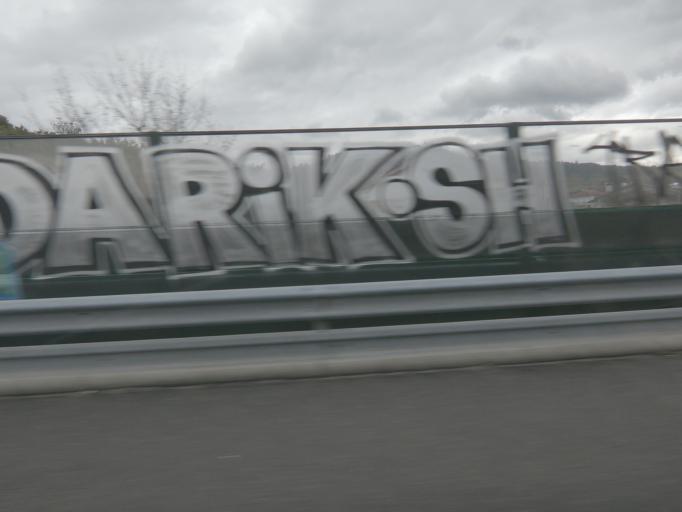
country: ES
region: Galicia
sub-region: Provincia de Ourense
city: Punxin
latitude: 42.3513
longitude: -7.9974
